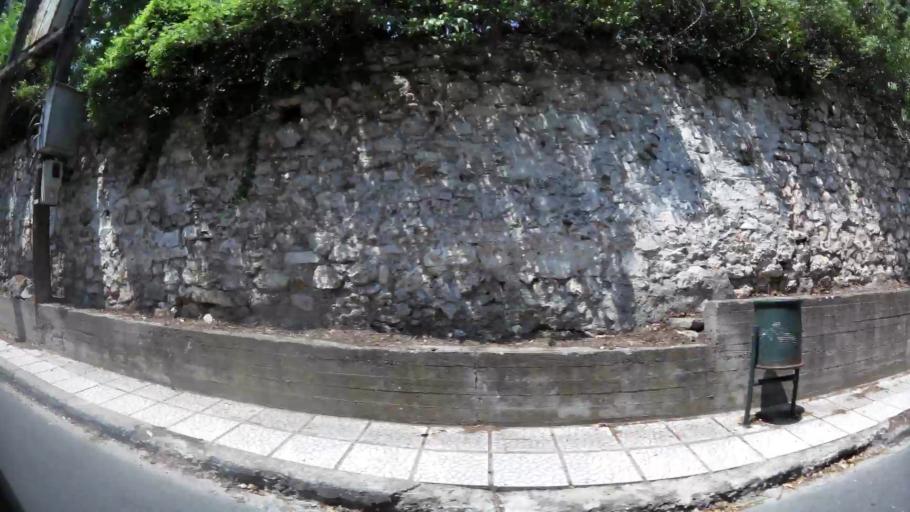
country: GR
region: Central Macedonia
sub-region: Nomos Imathias
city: Veroia
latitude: 40.5164
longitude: 22.1949
